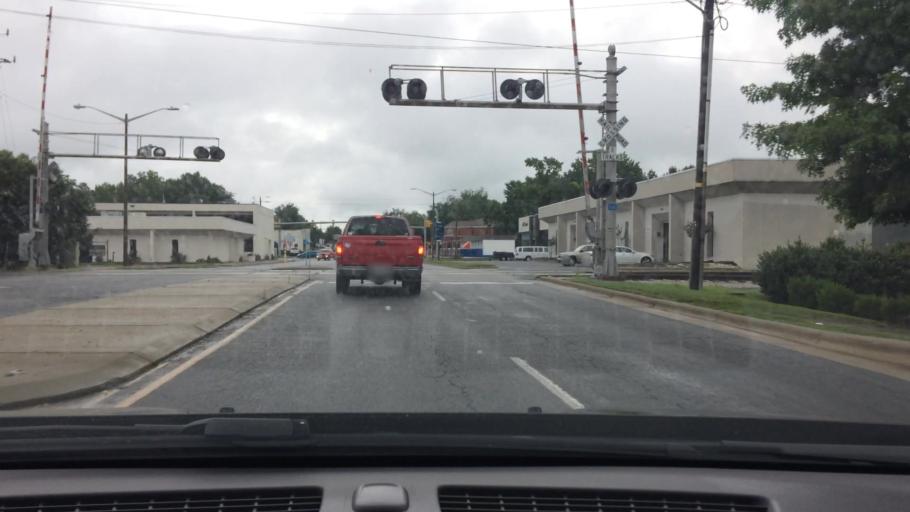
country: US
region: North Carolina
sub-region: Pitt County
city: Greenville
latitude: 35.6005
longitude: -77.3754
